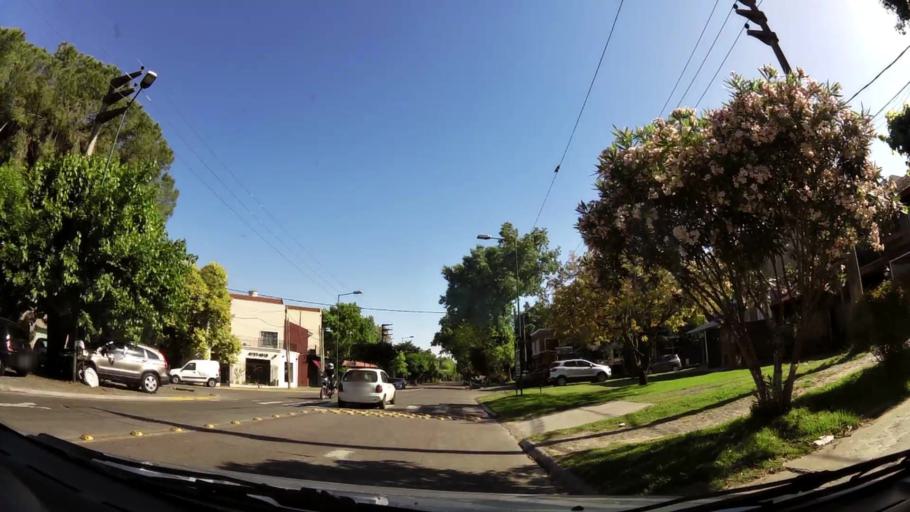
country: AR
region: Buenos Aires
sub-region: Partido de San Isidro
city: San Isidro
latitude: -34.4826
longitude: -58.5557
